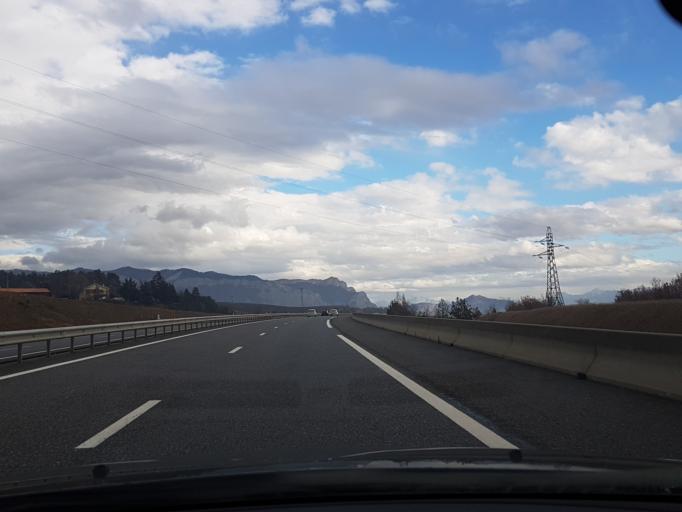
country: FR
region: Provence-Alpes-Cote d'Azur
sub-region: Departement des Hautes-Alpes
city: Laragne-Monteglin
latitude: 44.3353
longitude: 5.8984
